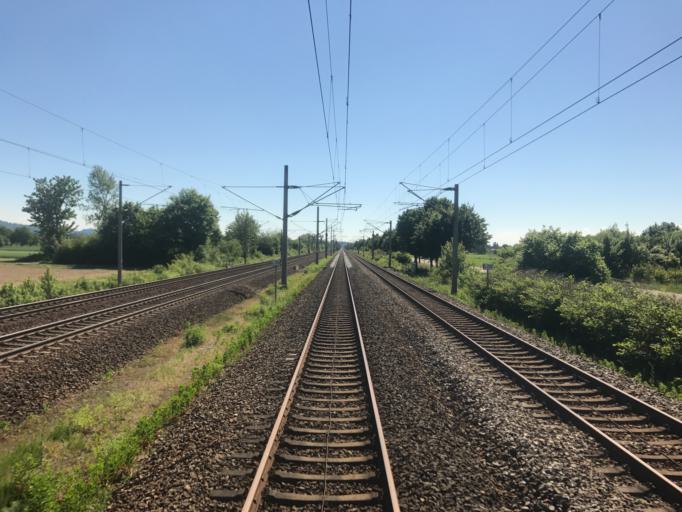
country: DE
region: Baden-Wuerttemberg
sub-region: Karlsruhe Region
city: Ottersweier
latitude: 48.6643
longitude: 8.0982
